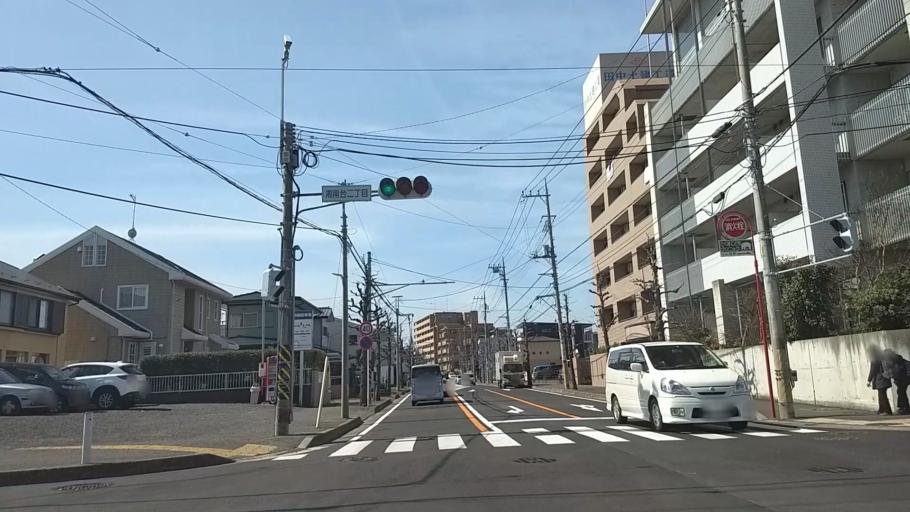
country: JP
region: Kanagawa
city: Fujisawa
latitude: 35.3925
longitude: 139.4664
